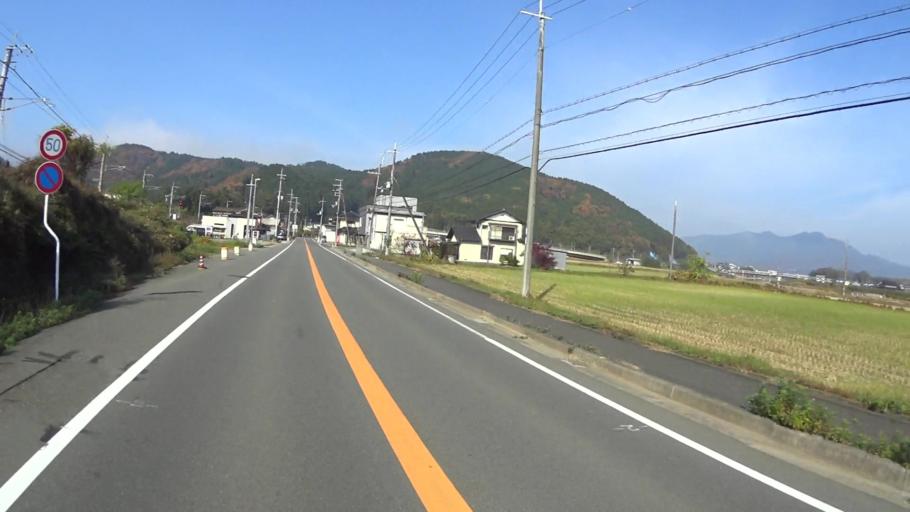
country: JP
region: Kyoto
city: Fukuchiyama
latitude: 35.2751
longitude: 135.1394
